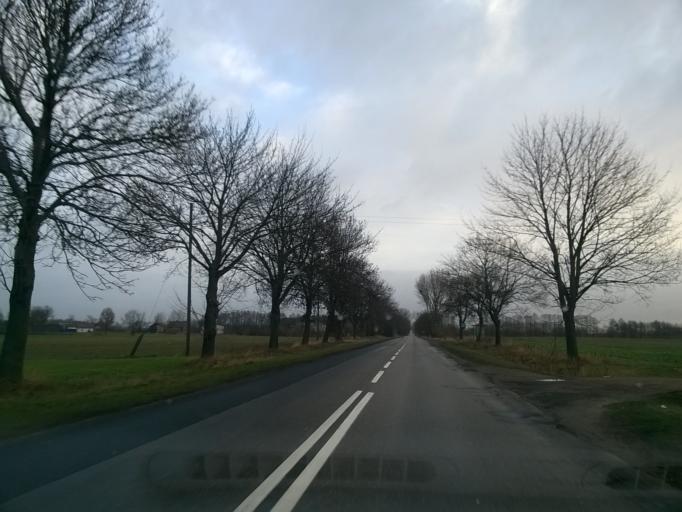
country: PL
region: Greater Poland Voivodeship
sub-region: Powiat wagrowiecki
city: Wagrowiec
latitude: 52.8537
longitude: 17.2689
